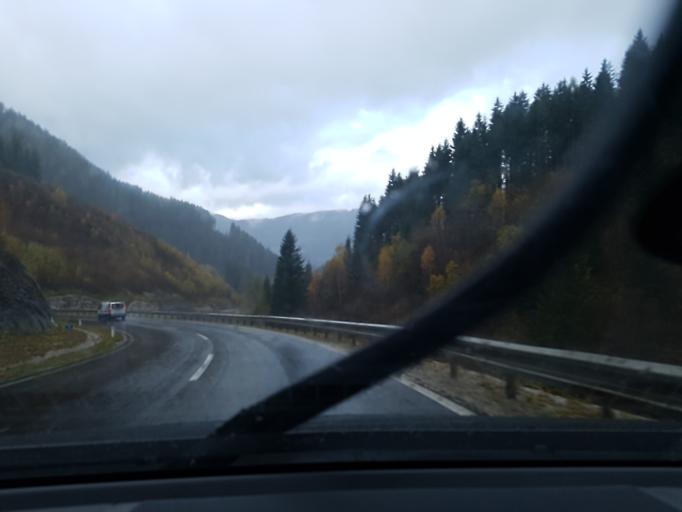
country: AT
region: Styria
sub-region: Politischer Bezirk Liezen
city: Trieben
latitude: 47.4749
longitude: 14.4849
